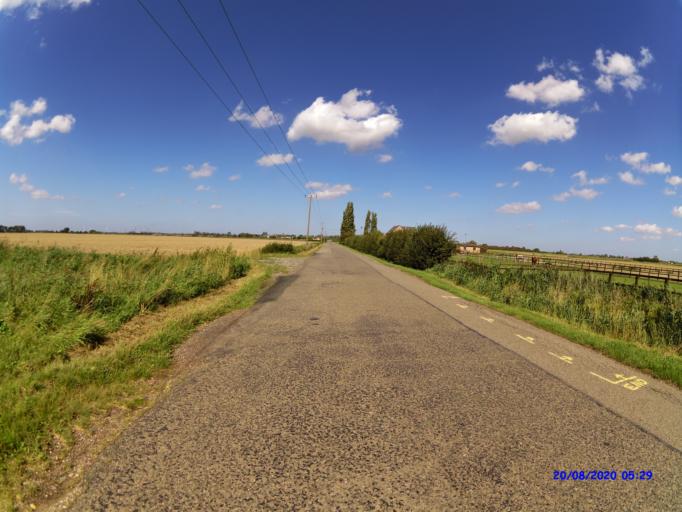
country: GB
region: England
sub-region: Cambridgeshire
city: Whittlesey
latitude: 52.5370
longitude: -0.1073
